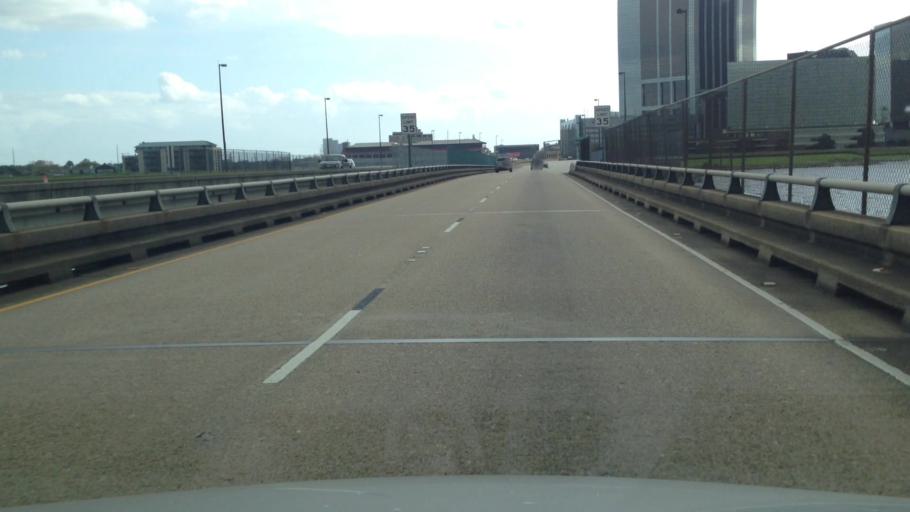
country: US
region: Louisiana
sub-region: Jefferson Parish
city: Metairie
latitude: 30.0237
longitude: -90.1538
